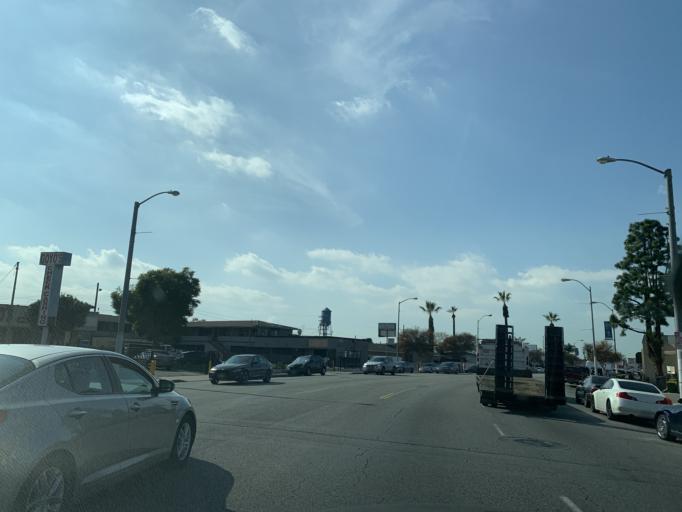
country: US
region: California
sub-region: Los Angeles County
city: Lynwood
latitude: 33.9306
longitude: -118.2049
